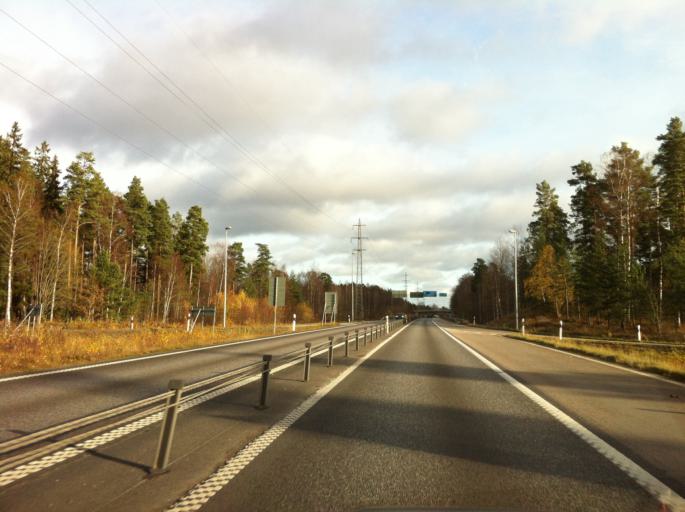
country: SE
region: Kronoberg
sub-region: Vaxjo Kommun
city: Gemla
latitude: 56.8330
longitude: 14.6985
